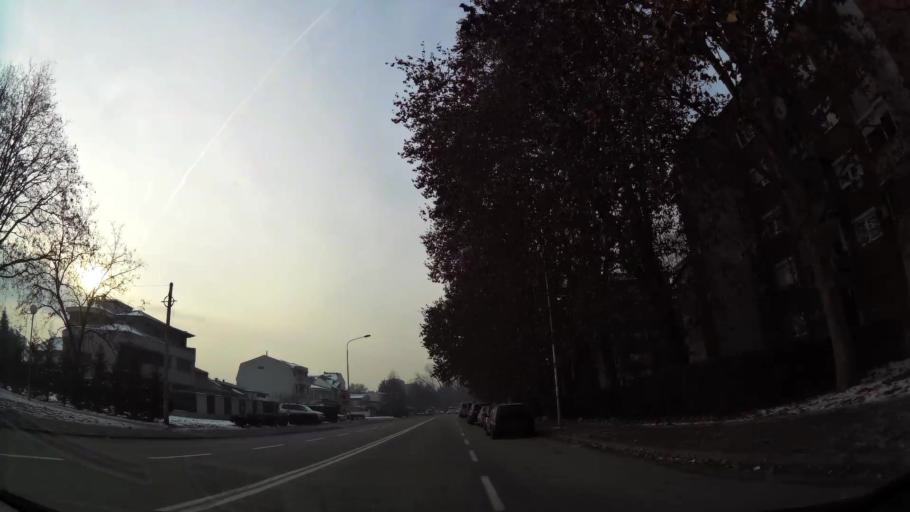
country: MK
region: Butel
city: Butel
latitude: 42.0244
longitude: 21.4446
